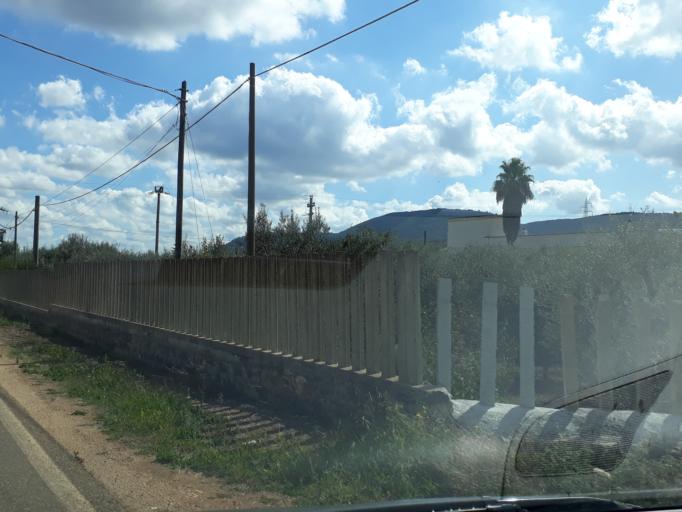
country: IT
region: Apulia
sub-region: Provincia di Brindisi
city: Pezze di Greco
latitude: 40.8026
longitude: 17.3968
